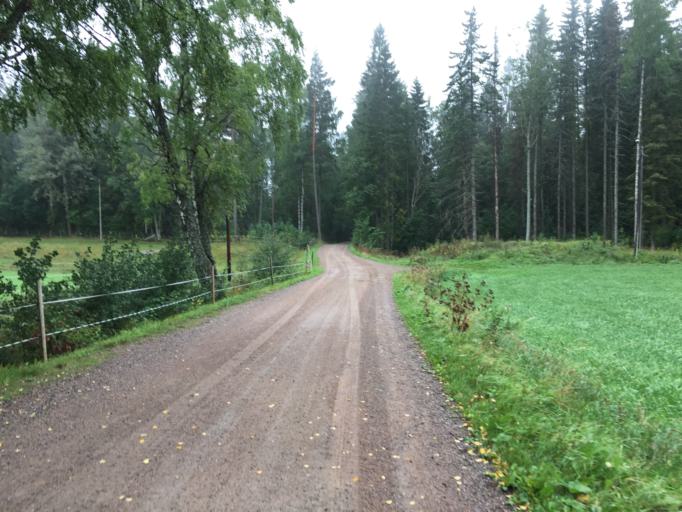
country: NO
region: Akershus
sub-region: Baerum
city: Lysaker
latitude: 59.9762
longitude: 10.6344
